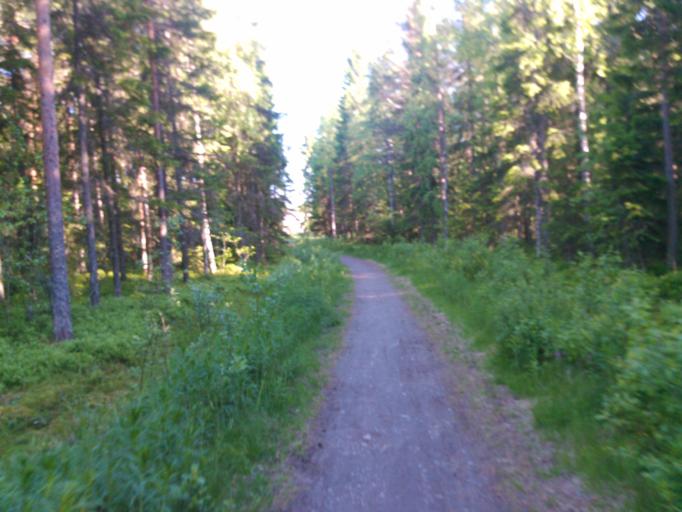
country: SE
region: Vaesterbotten
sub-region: Umea Kommun
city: Ersmark
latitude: 63.8647
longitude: 20.3336
